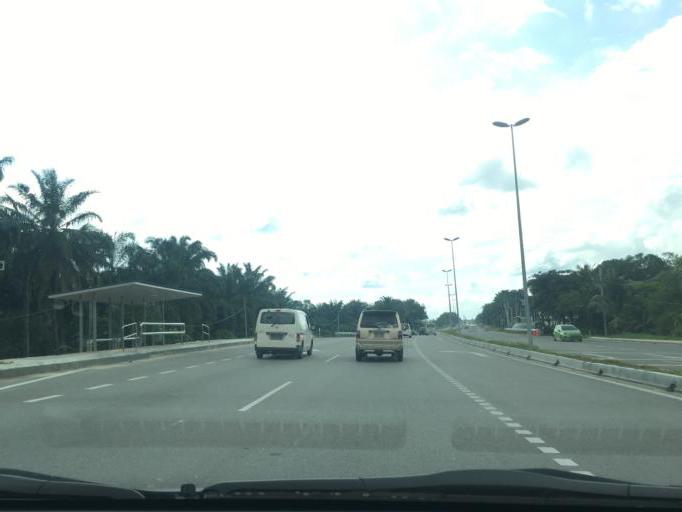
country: MY
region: Selangor
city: Batu Arang
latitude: 3.3035
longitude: 101.4312
